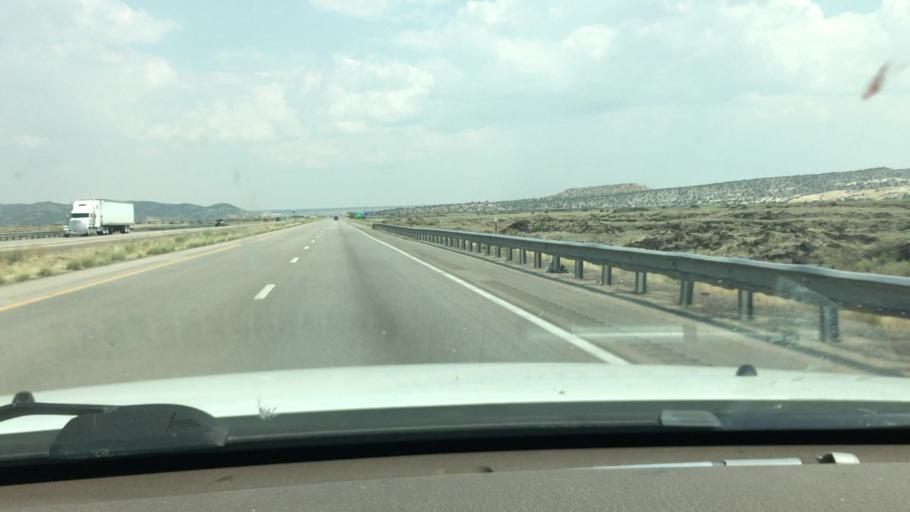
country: US
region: New Mexico
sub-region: Cibola County
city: Grants
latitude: 35.0955
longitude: -107.7867
